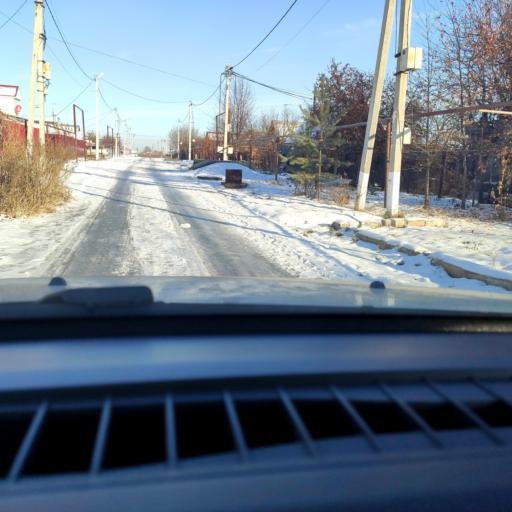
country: RU
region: Samara
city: Podstepki
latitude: 53.5170
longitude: 49.1280
